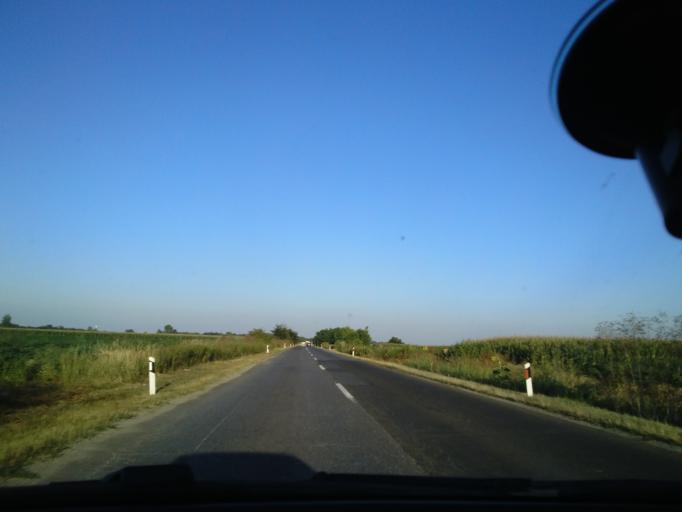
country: RS
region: Autonomna Pokrajina Vojvodina
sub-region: Juznobacki Okrug
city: Backi Petrovac
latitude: 45.3396
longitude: 19.6555
